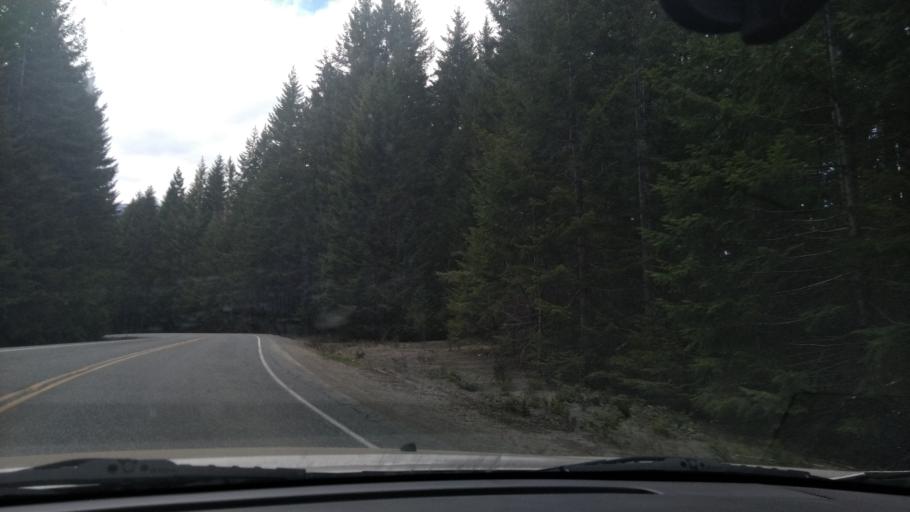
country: CA
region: British Columbia
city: Campbell River
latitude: 49.8711
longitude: -125.6527
